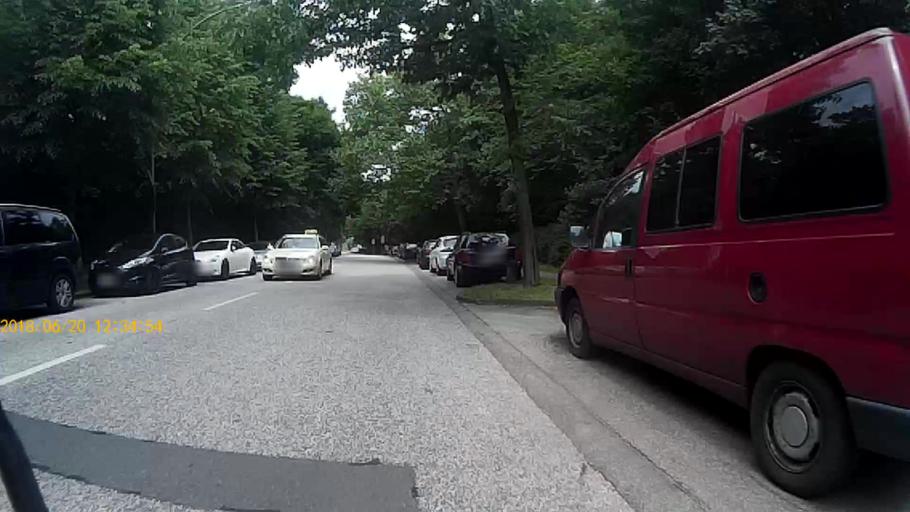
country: DE
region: Hamburg
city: Harburg
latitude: 53.4666
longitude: 9.9667
